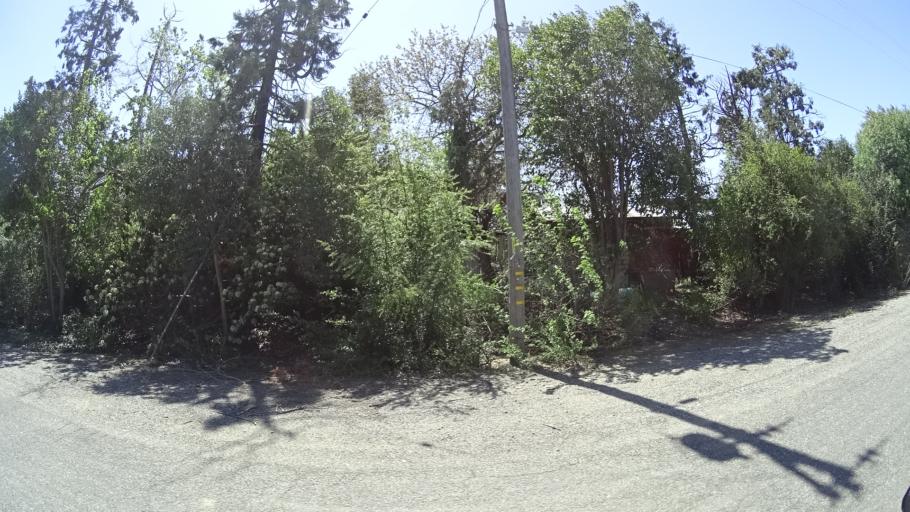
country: US
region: California
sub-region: Glenn County
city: Orland
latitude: 39.7977
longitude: -122.1696
